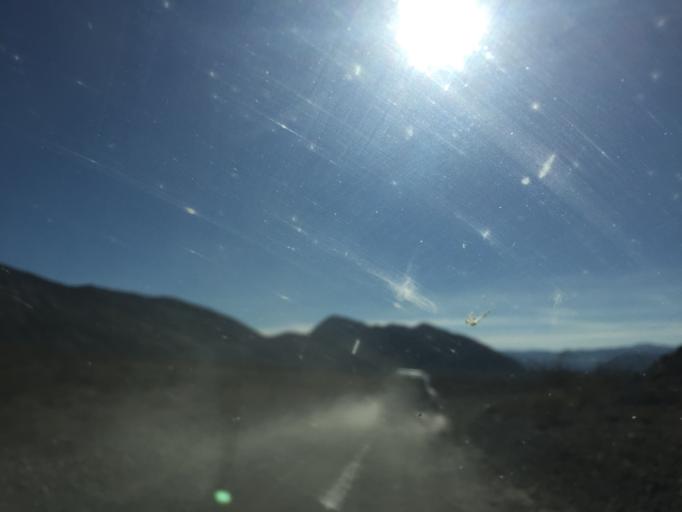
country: US
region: California
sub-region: Inyo County
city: Lone Pine
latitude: 36.7876
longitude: -117.5195
